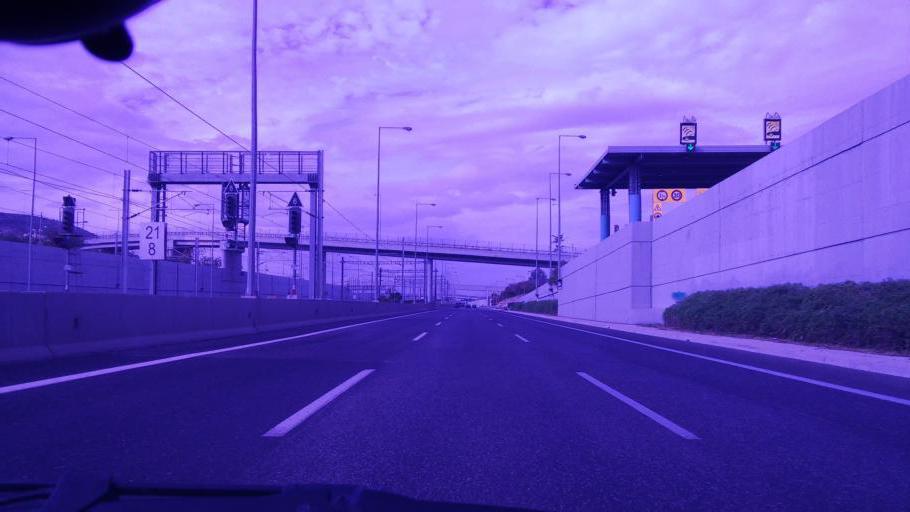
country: GR
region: Attica
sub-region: Nomarchia Dytikis Attikis
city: Zefyri
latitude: 38.0711
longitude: 23.7090
